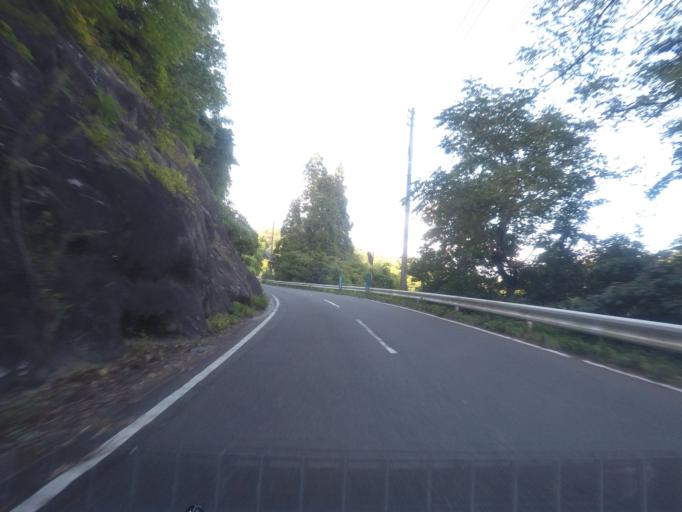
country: JP
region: Fukushima
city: Fukushima-shi
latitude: 37.7194
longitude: 140.5148
